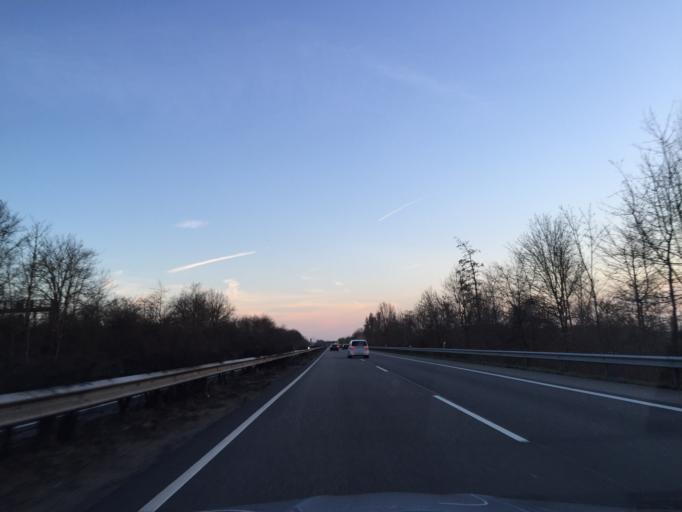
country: DE
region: Baden-Wuerttemberg
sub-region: Karlsruhe Region
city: Hockenheim
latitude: 49.3153
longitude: 8.5355
